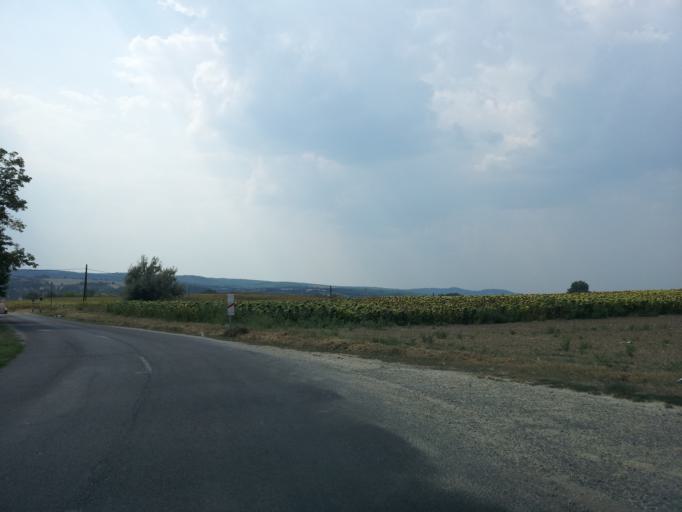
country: HU
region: Gyor-Moson-Sopron
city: Pannonhalma
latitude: 47.5615
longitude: 17.7299
